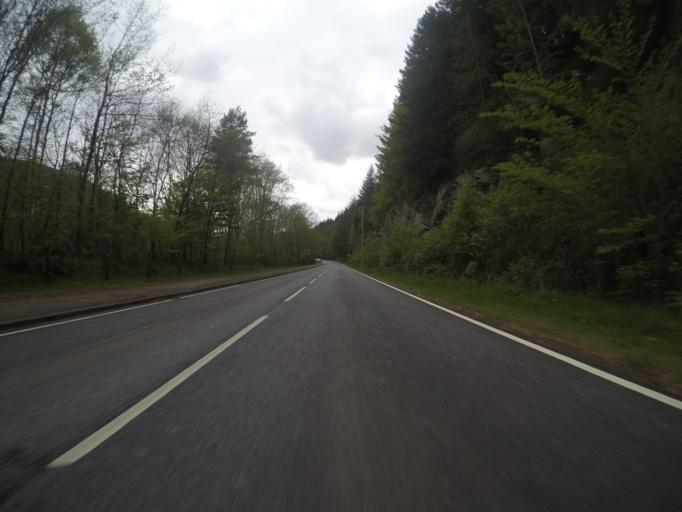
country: GB
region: Scotland
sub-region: Highland
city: Beauly
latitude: 57.2165
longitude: -4.6233
